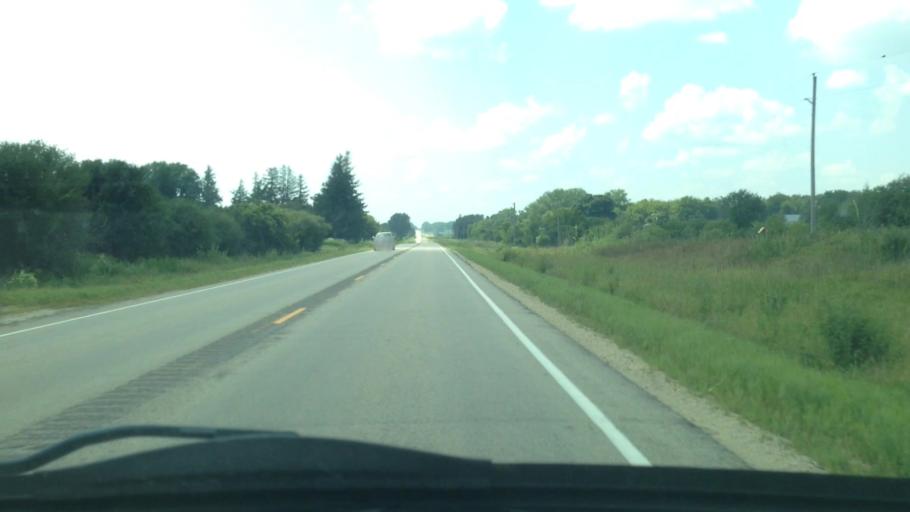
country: US
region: Minnesota
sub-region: Olmsted County
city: Stewartville
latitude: 43.8556
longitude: -92.4413
